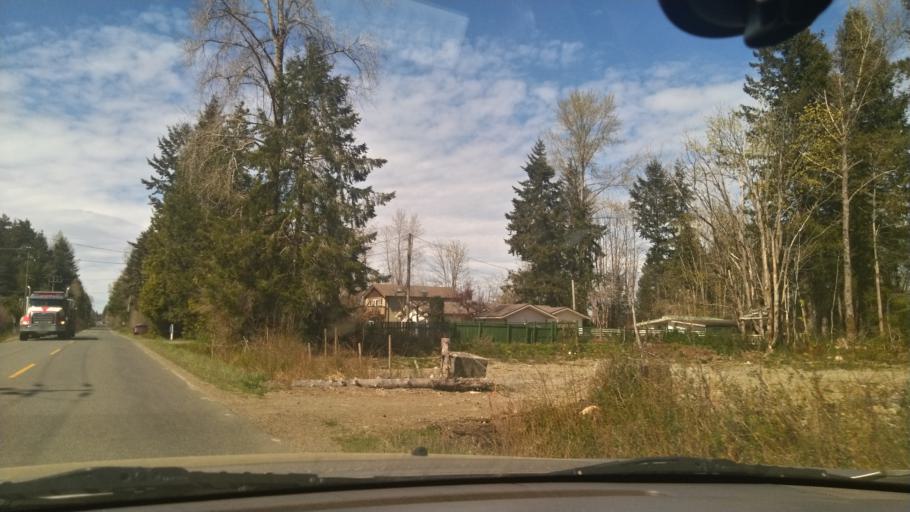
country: CA
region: British Columbia
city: Courtenay
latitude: 49.7000
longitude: -125.0171
